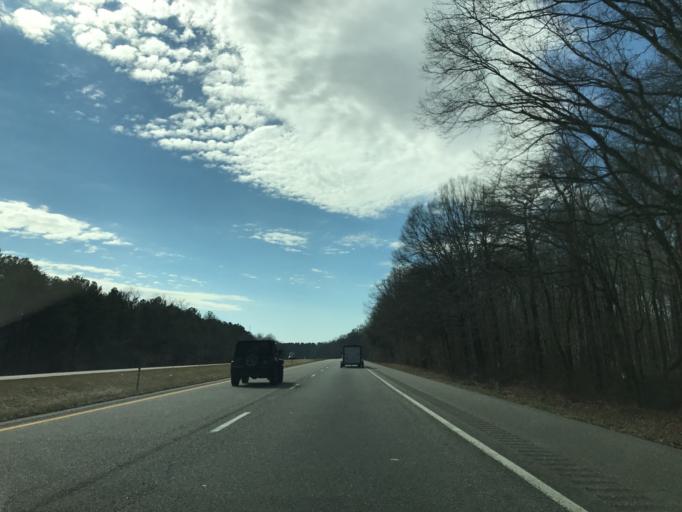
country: US
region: Delaware
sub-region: New Castle County
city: Townsend
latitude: 39.3299
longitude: -75.8416
